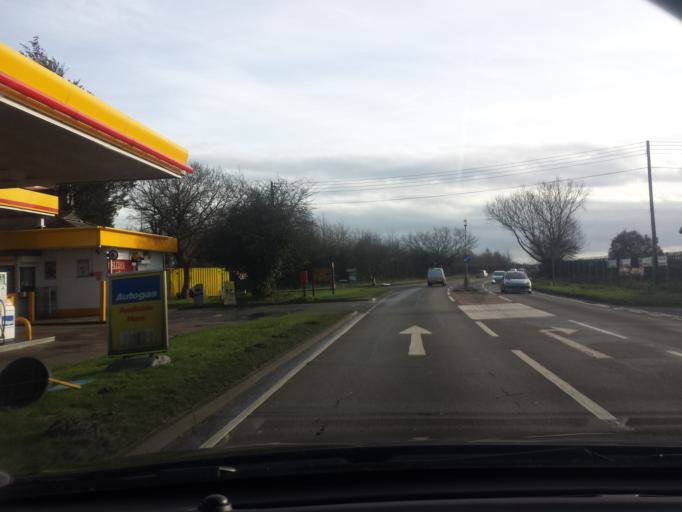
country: GB
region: England
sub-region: Essex
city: Great Bentley
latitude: 51.8686
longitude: 1.0745
